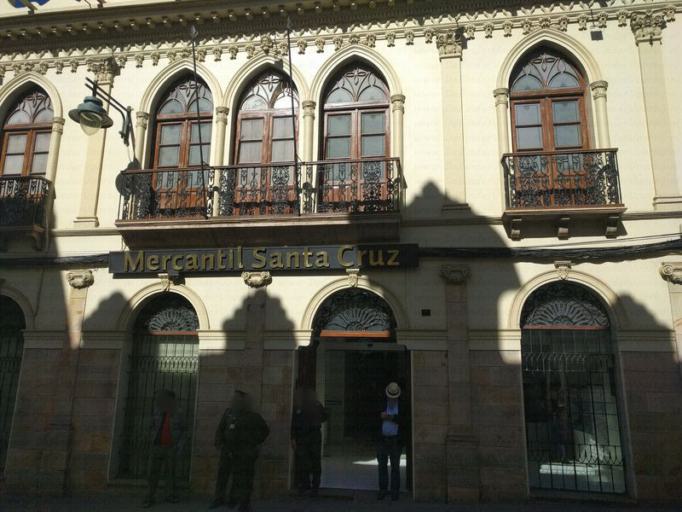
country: BO
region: Chuquisaca
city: Sucre
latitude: -19.0430
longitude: -65.2553
